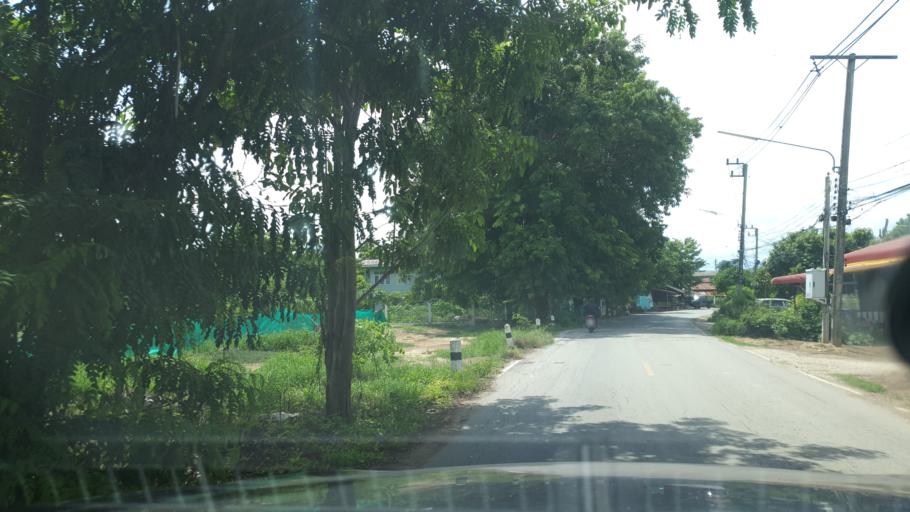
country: TH
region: Sukhothai
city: Sukhothai
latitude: 16.9953
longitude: 99.8482
